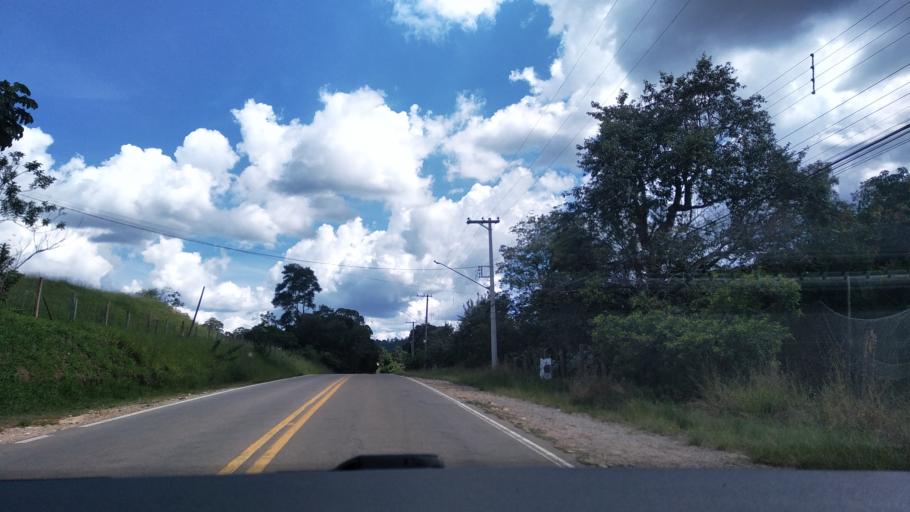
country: BR
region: Sao Paulo
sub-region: Varzea Paulista
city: Varzea Paulista
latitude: -23.2578
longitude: -46.8799
